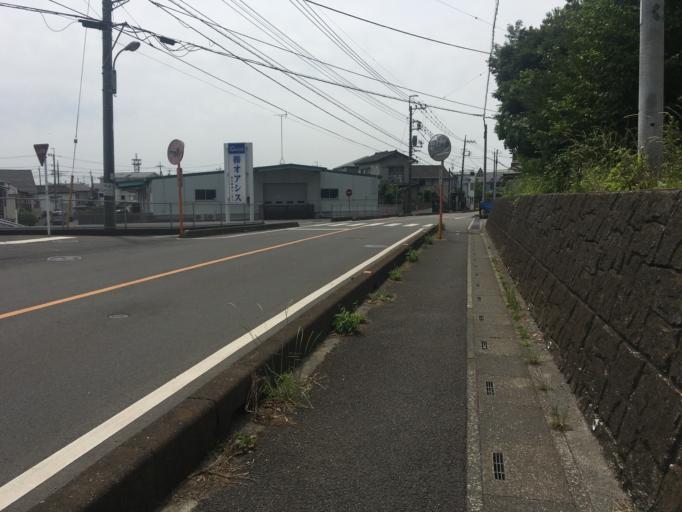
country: JP
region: Saitama
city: Sayama
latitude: 35.8441
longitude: 139.4258
